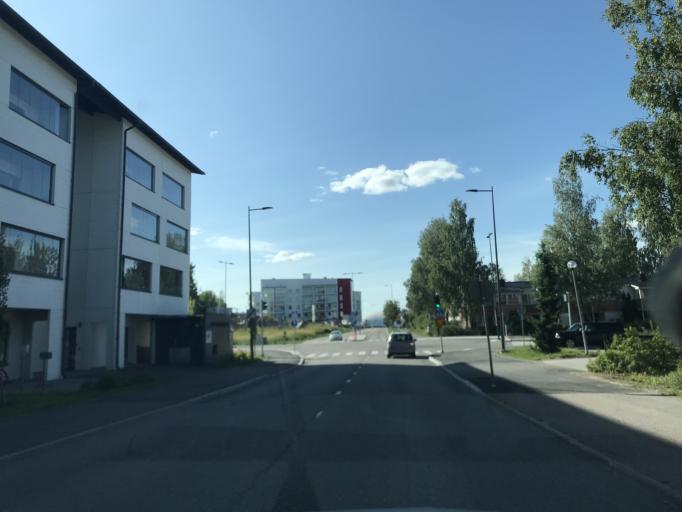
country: FI
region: Uusimaa
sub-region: Helsinki
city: Nurmijaervi
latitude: 60.3798
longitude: 24.7463
